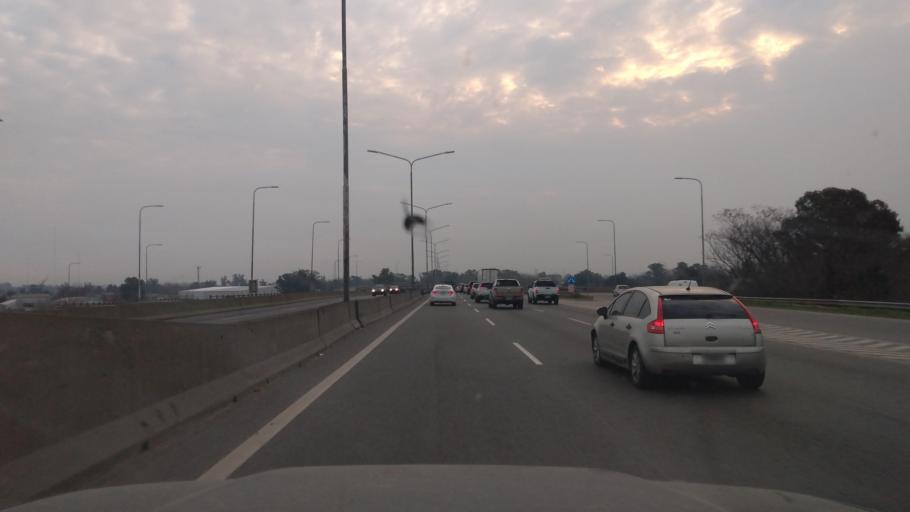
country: AR
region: Buenos Aires
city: Hurlingham
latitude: -34.5684
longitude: -58.6501
